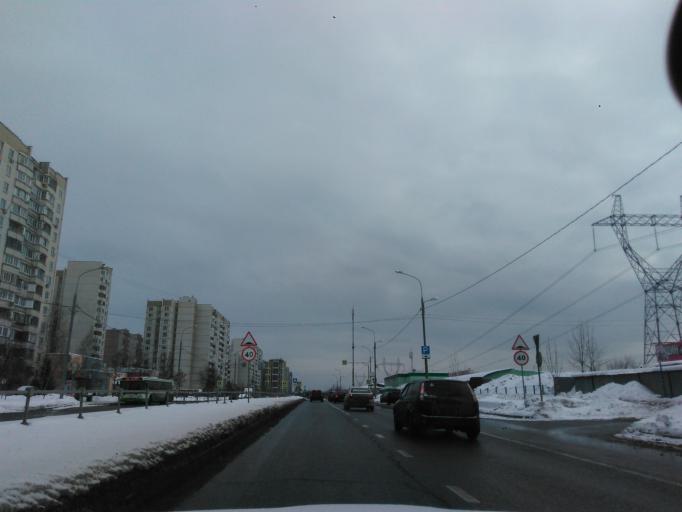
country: RU
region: Moskovskaya
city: Andreyevka
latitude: 55.9755
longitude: 37.1490
